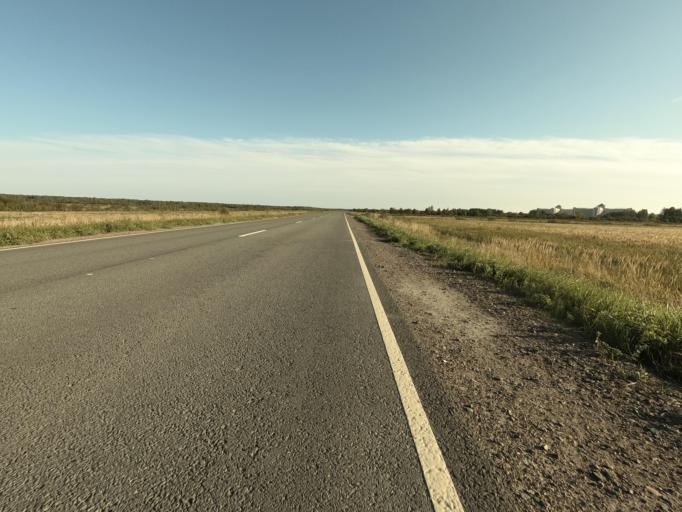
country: RU
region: St.-Petersburg
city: Sapernyy
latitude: 59.7526
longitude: 30.6352
